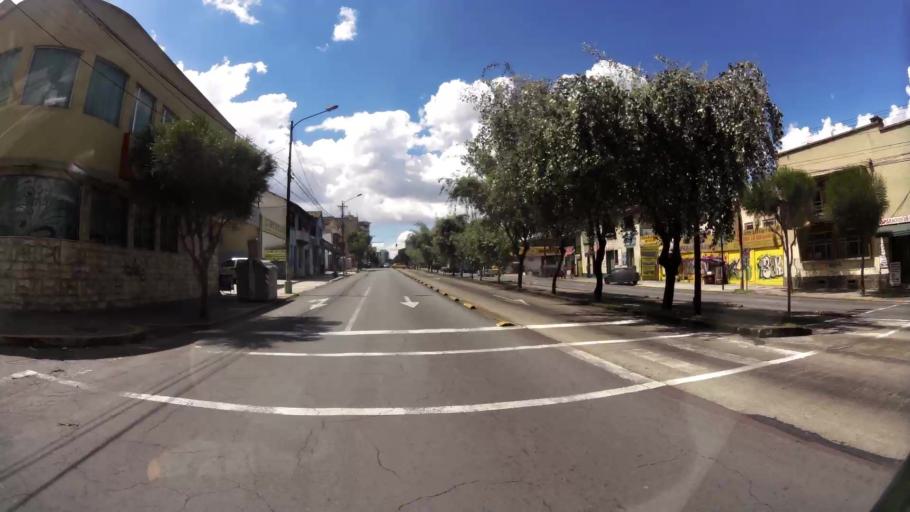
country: EC
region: Pichincha
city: Quito
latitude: -0.1928
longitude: -78.4981
